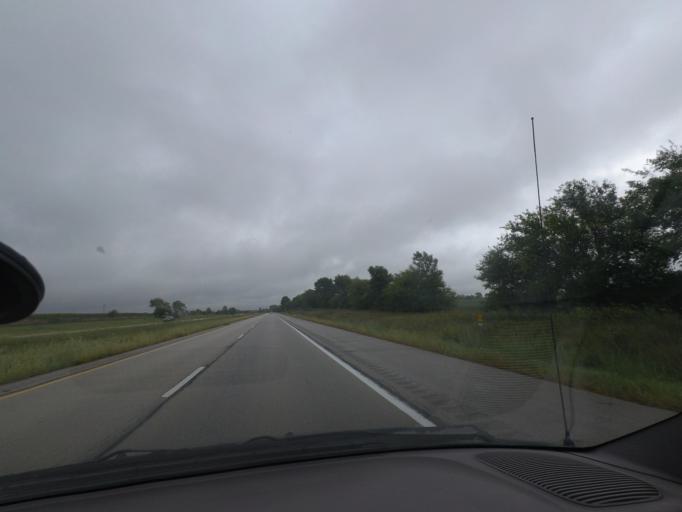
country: US
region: Illinois
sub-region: Piatt County
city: Monticello
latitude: 40.0909
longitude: -88.5130
